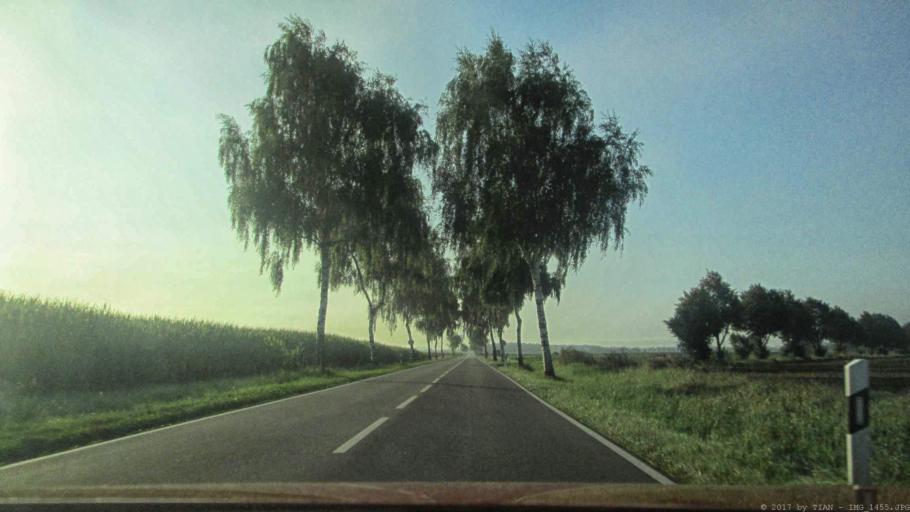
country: DE
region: Lower Saxony
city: Wittingen
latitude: 52.7531
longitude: 10.7206
